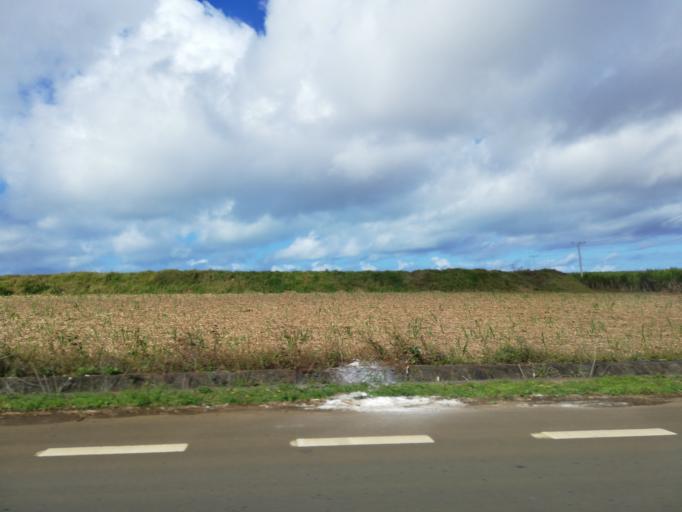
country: MU
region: Grand Port
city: Plaine Magnien
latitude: -20.4111
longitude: 57.6737
